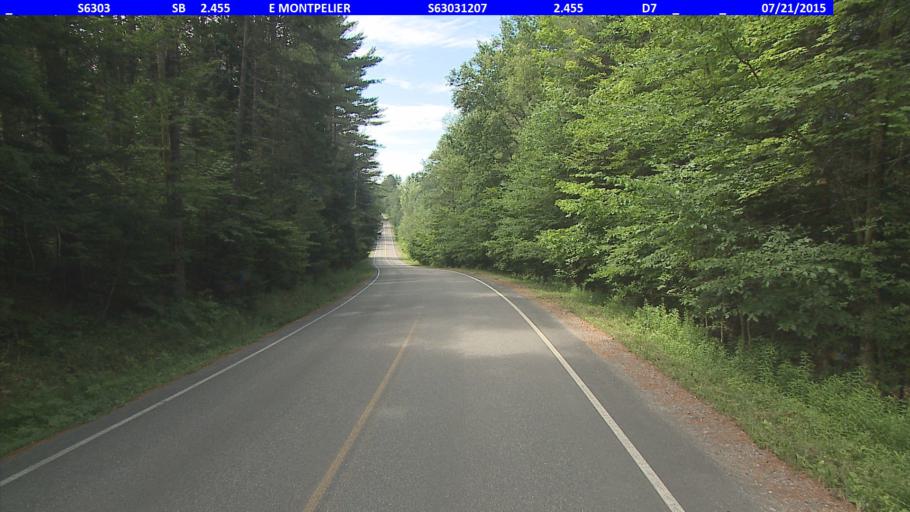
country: US
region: Vermont
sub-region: Washington County
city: Montpelier
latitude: 44.3033
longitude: -72.5325
